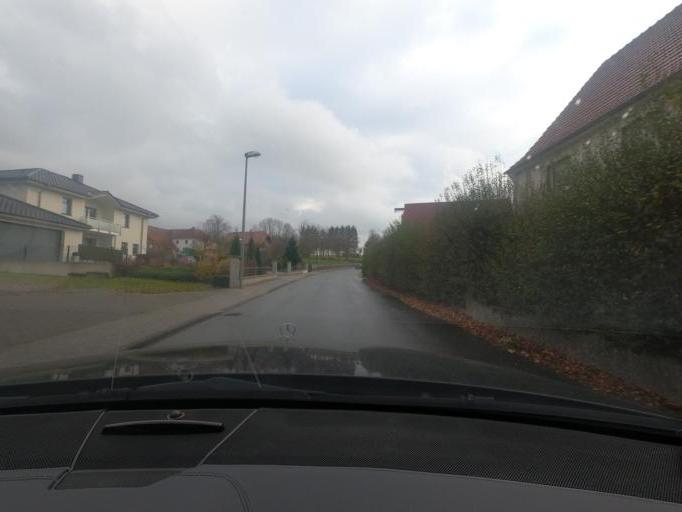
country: DE
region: North Rhine-Westphalia
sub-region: Regierungsbezirk Detmold
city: Wunnenberg
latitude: 51.5722
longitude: 8.7706
